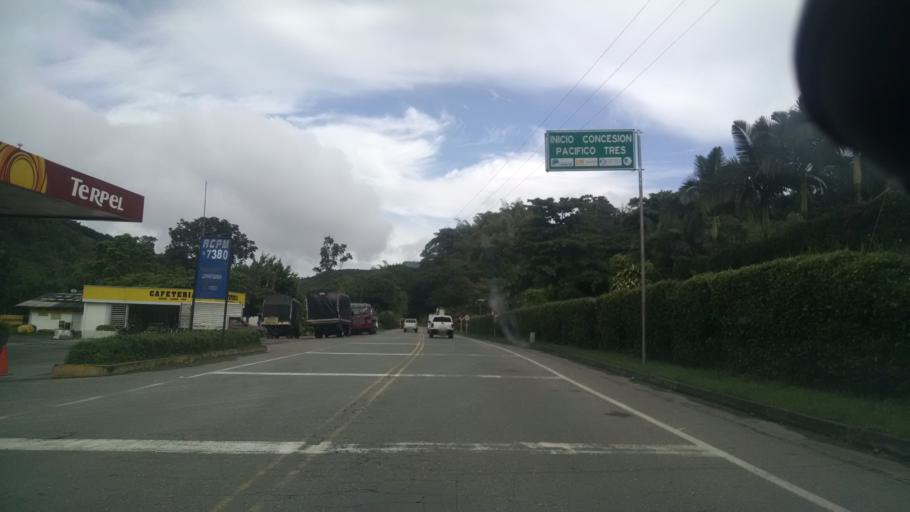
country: CO
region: Caldas
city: Palestina
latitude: 5.0590
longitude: -75.6079
